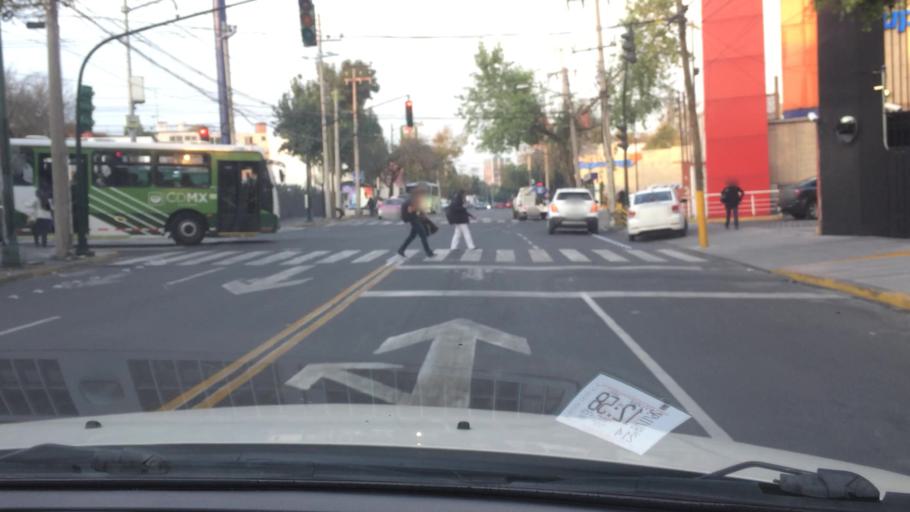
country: MX
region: Mexico City
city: Alvaro Obregon
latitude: 19.3575
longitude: -99.1986
